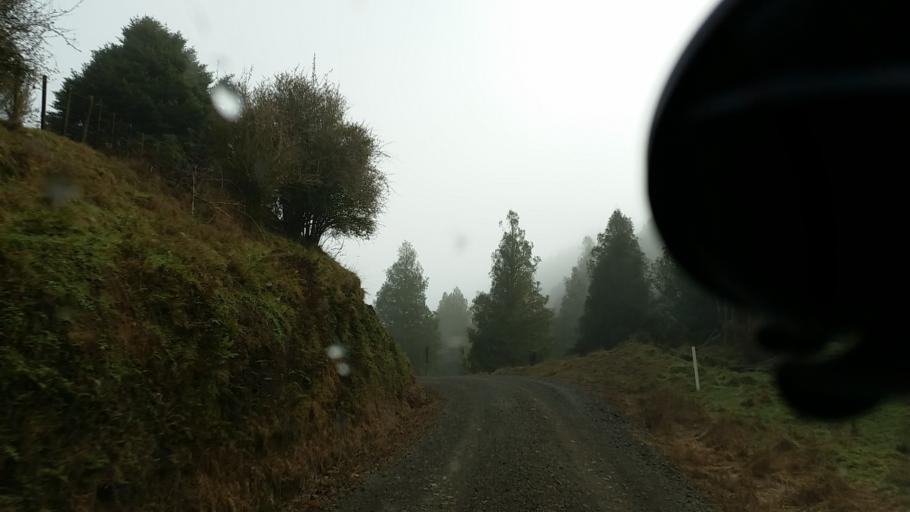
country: NZ
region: Taranaki
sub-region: New Plymouth District
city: Waitara
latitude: -38.9708
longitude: 174.7989
